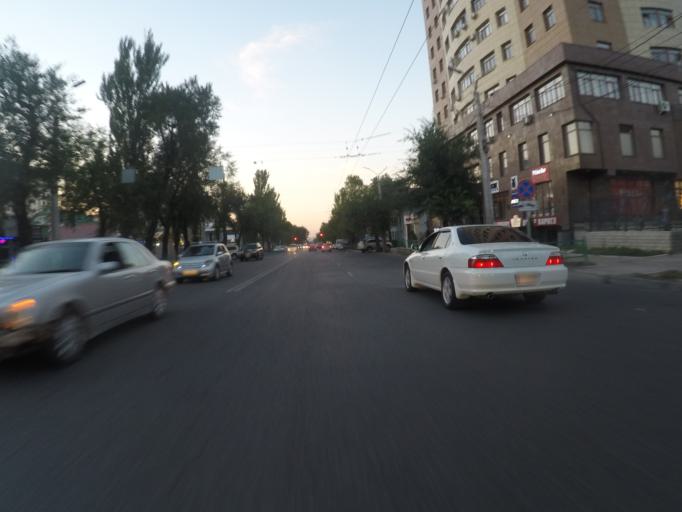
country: KG
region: Chuy
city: Bishkek
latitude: 42.8549
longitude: 74.6101
